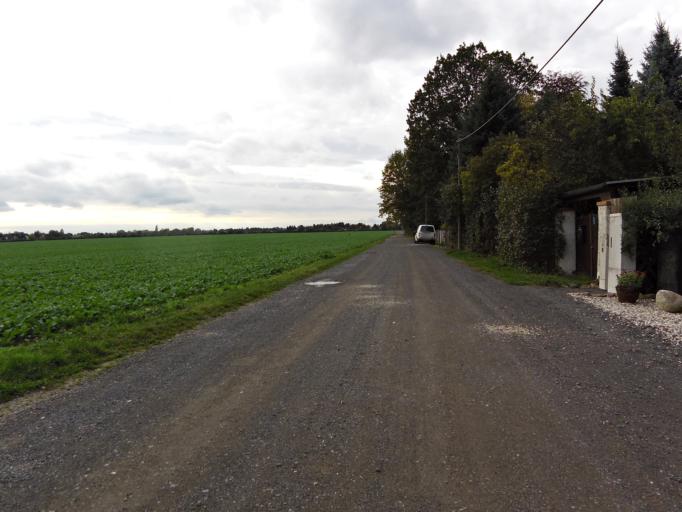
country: DE
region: Saxony
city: Grossposna
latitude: 51.2944
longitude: 12.4748
